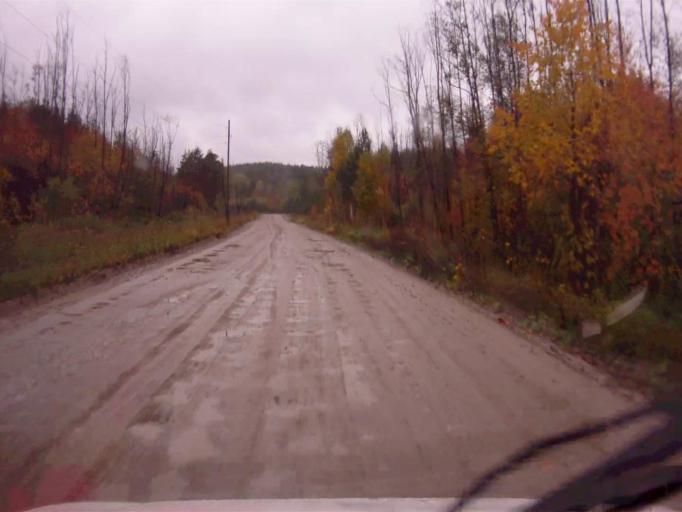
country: RU
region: Chelyabinsk
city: Kyshtym
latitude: 55.7403
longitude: 60.5100
